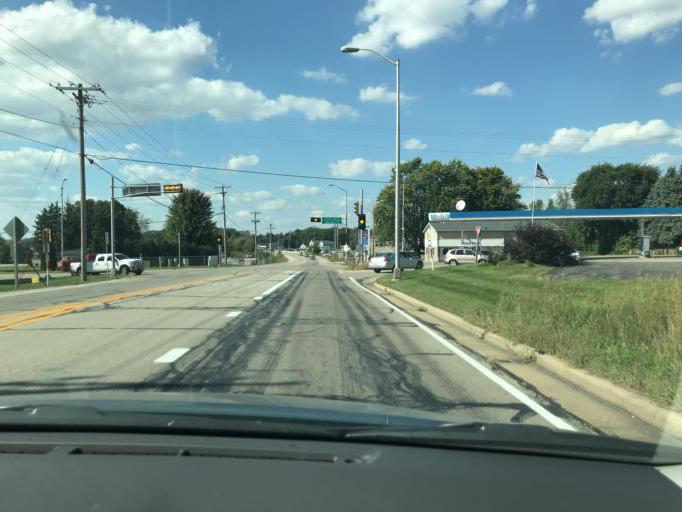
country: US
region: Wisconsin
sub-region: Walworth County
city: Williams Bay
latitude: 42.6185
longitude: -88.5806
